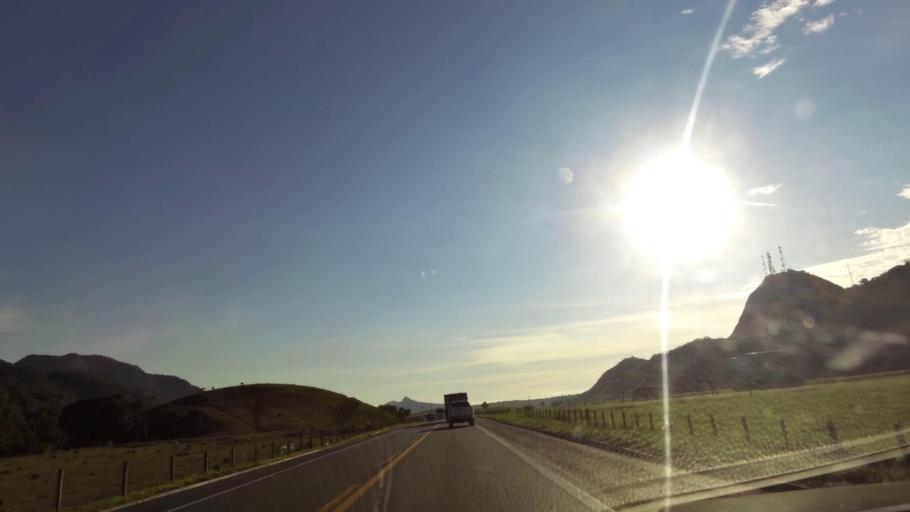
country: BR
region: Espirito Santo
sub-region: Guarapari
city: Guarapari
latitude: -20.6200
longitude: -40.5186
